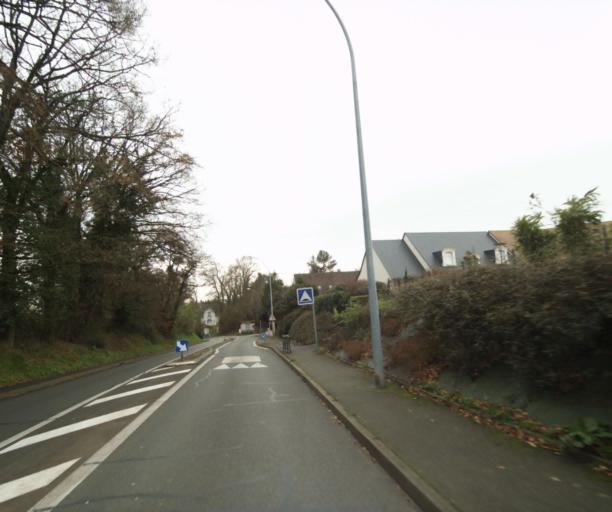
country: FR
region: Pays de la Loire
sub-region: Departement de la Sarthe
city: Le Mans
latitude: 48.0041
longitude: 0.2223
